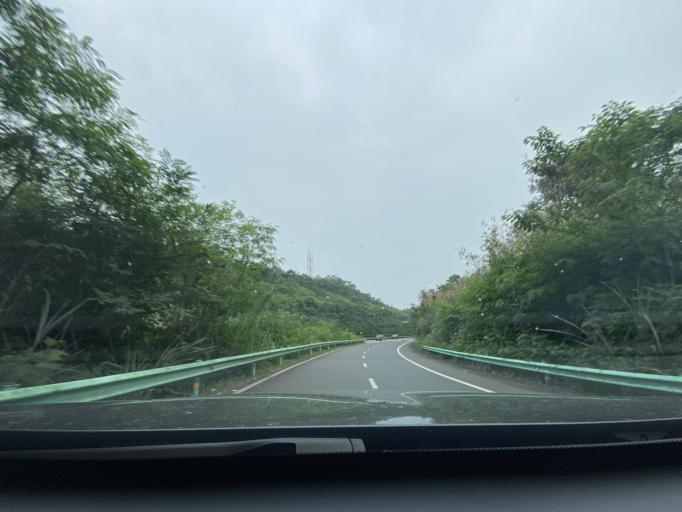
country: CN
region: Sichuan
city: Wenlin
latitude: 30.2976
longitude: 104.1233
